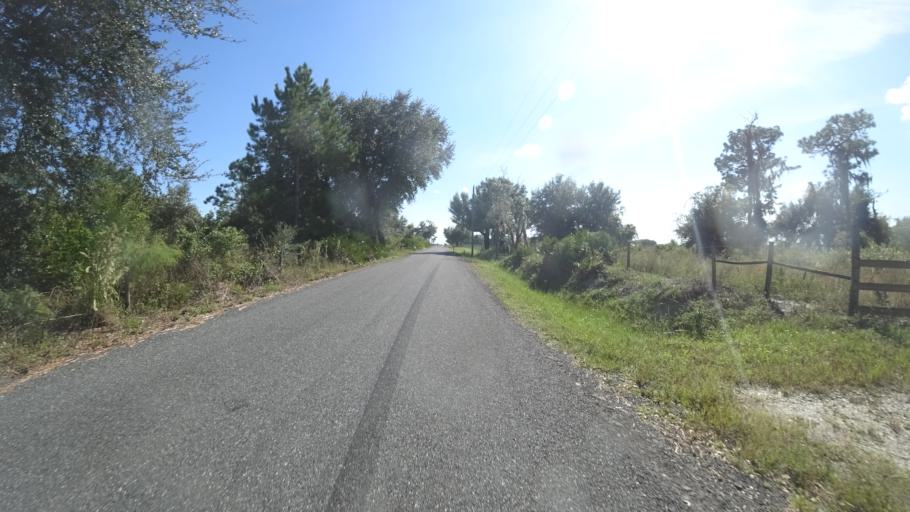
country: US
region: Florida
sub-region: Sarasota County
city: The Meadows
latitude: 27.4448
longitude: -82.2870
